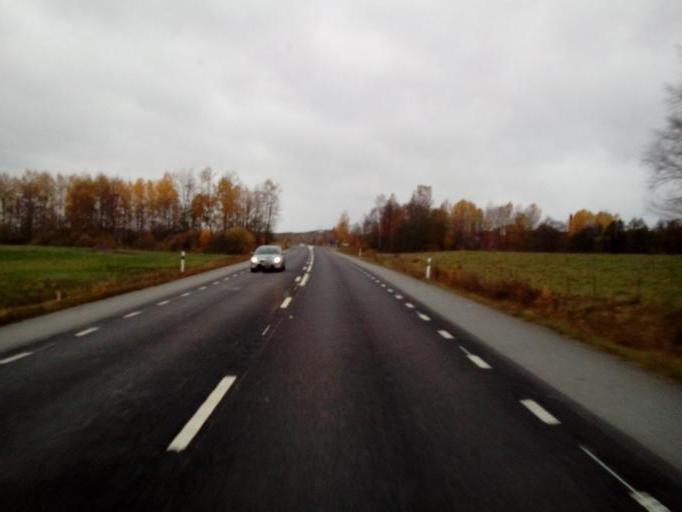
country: SE
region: OErebro
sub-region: Degerfors Kommun
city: Degerfors
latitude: 59.2842
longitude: 14.4617
